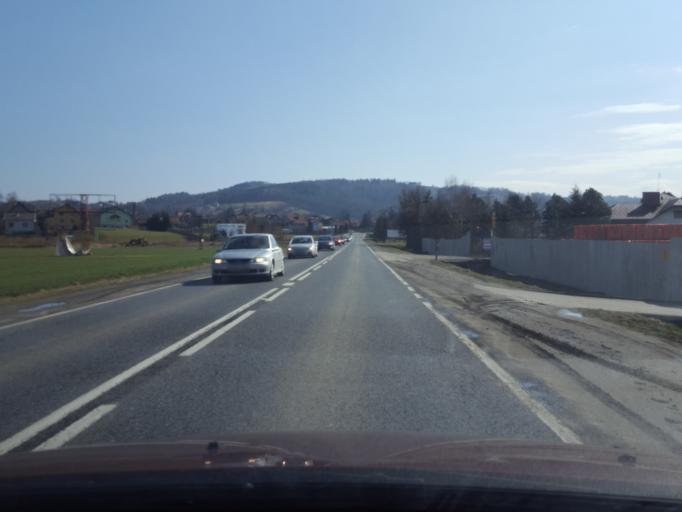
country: PL
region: Lesser Poland Voivodeship
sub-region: Powiat nowosadecki
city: Chelmiec
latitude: 49.6763
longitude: 20.6756
